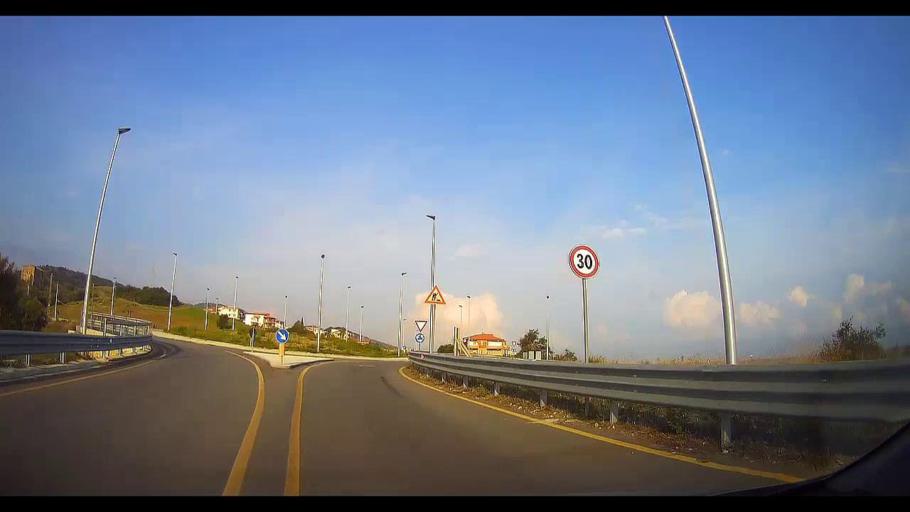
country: IT
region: Calabria
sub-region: Provincia di Cosenza
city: Cariati
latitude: 39.5234
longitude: 16.8972
